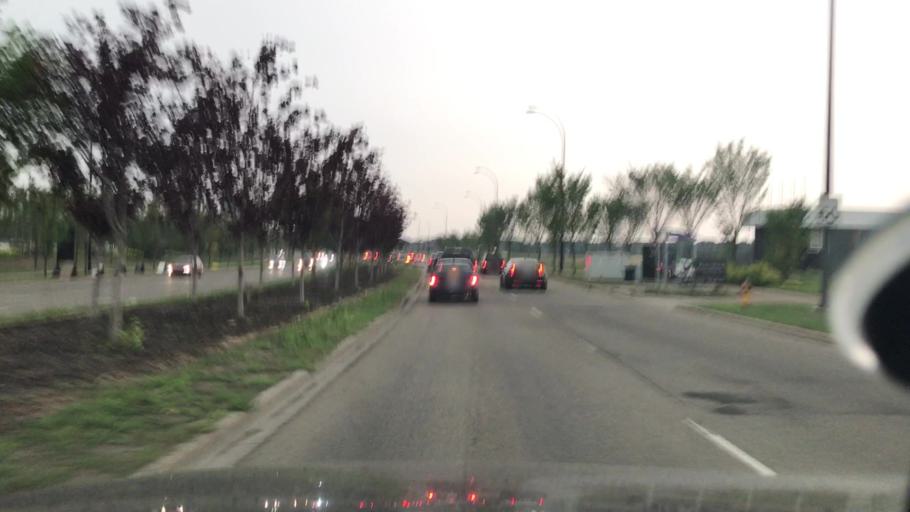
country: CA
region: Alberta
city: Devon
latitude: 53.4365
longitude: -113.6118
